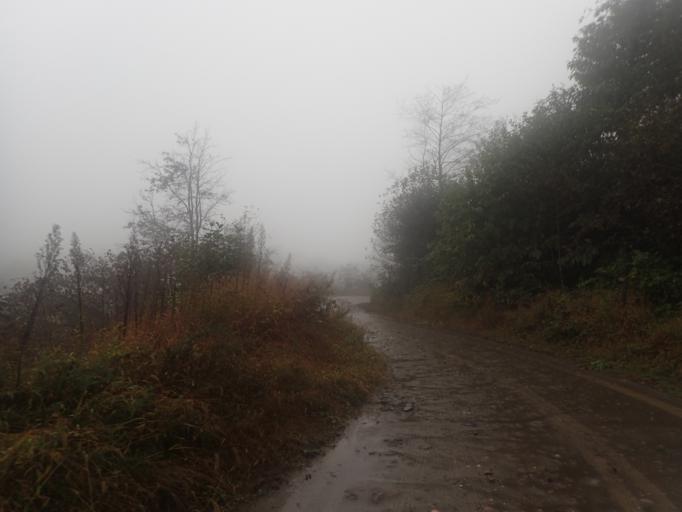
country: TR
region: Ordu
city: Persembe
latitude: 41.0223
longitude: 37.7041
